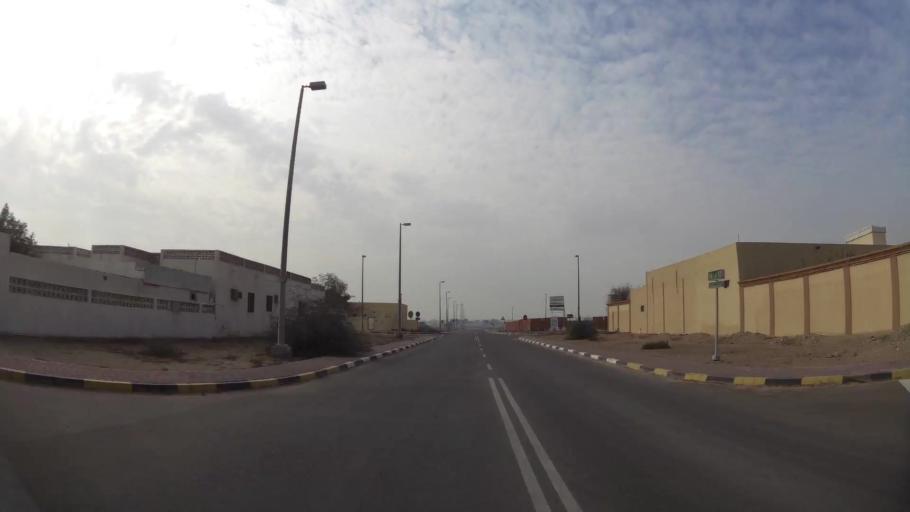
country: AE
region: Abu Dhabi
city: Abu Dhabi
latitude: 24.6800
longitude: 54.7754
